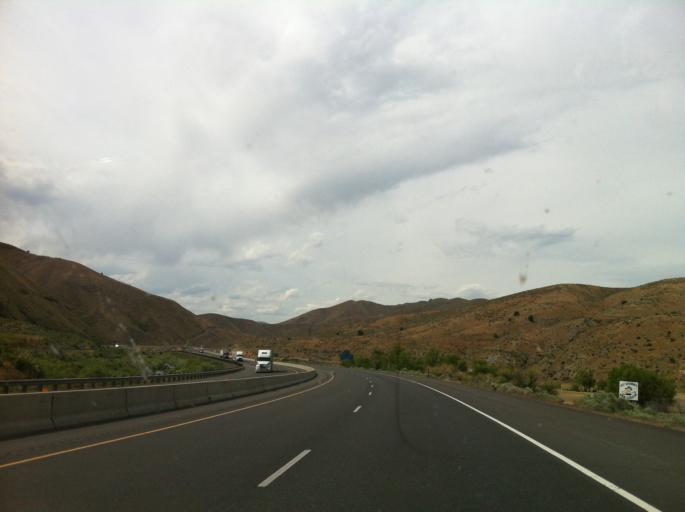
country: US
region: Idaho
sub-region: Washington County
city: Weiser
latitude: 44.4219
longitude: -117.3107
